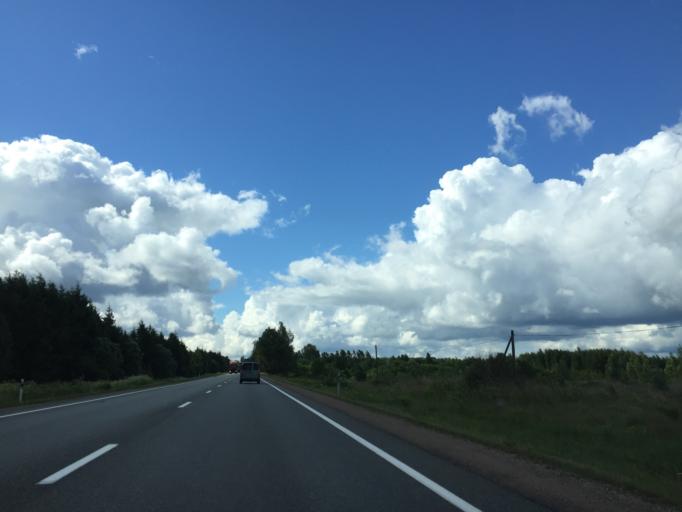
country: LV
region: Kekava
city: Kekava
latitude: 56.7924
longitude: 24.2434
